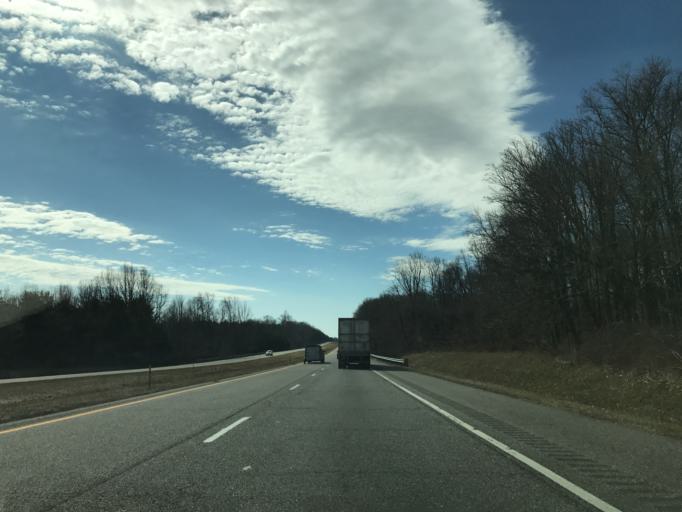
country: US
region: Delaware
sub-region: New Castle County
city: Townsend
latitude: 39.3427
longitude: -75.8313
